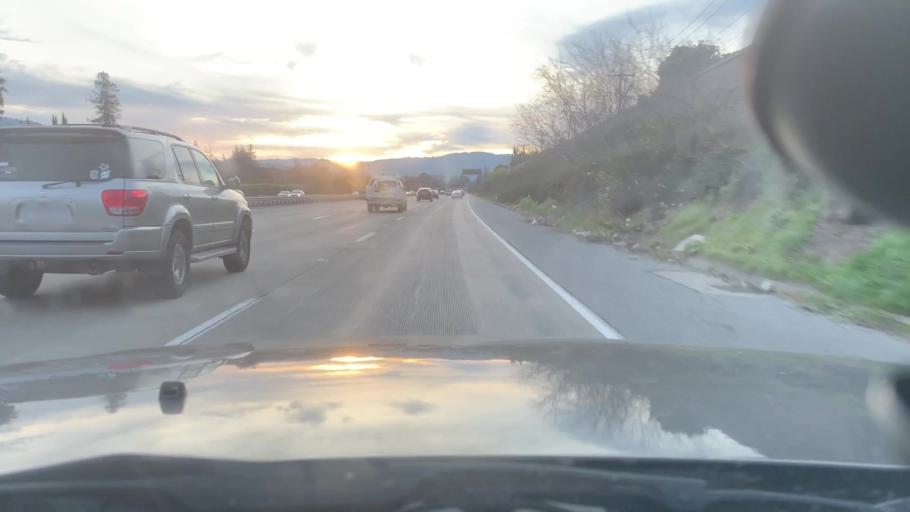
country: US
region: California
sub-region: Santa Clara County
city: Cambrian Park
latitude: 37.2538
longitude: -121.8828
